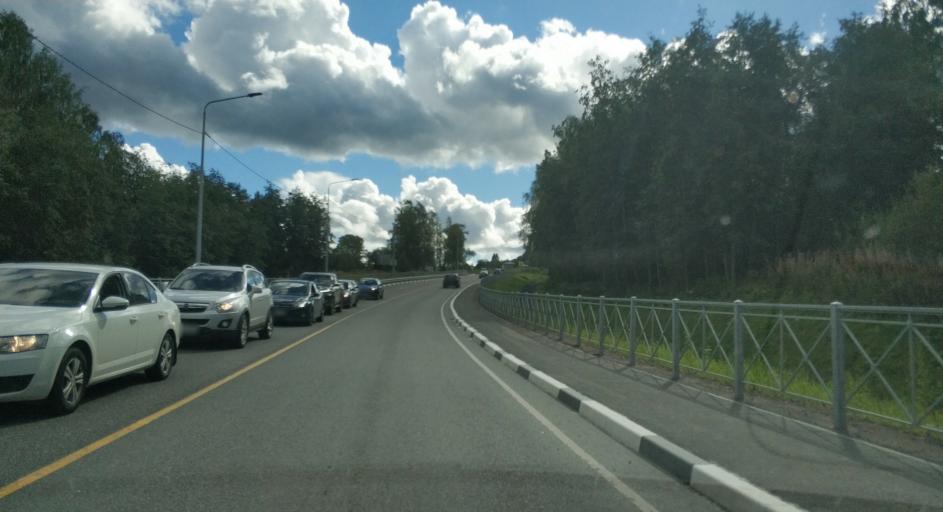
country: RU
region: Republic of Karelia
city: Ruskeala
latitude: 61.9365
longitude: 30.5905
